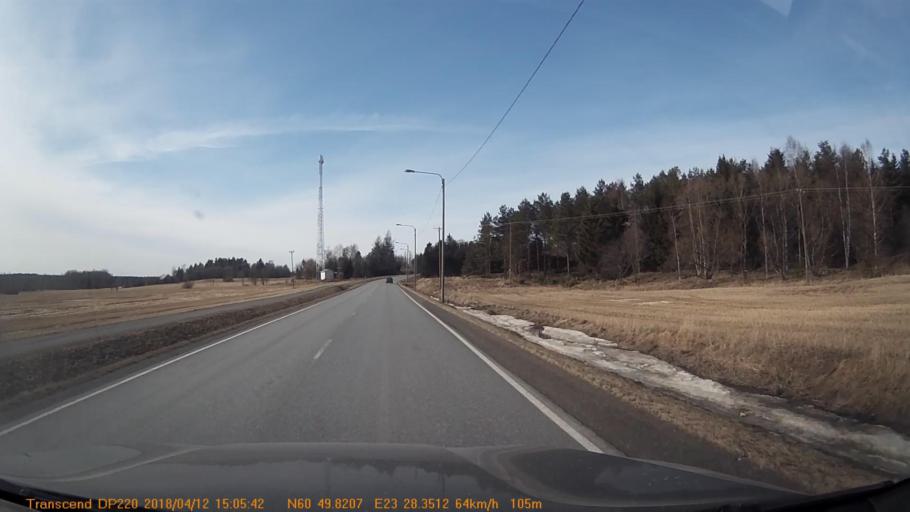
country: FI
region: Haeme
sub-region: Forssa
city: Jokioinen
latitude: 60.8305
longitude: 23.4722
